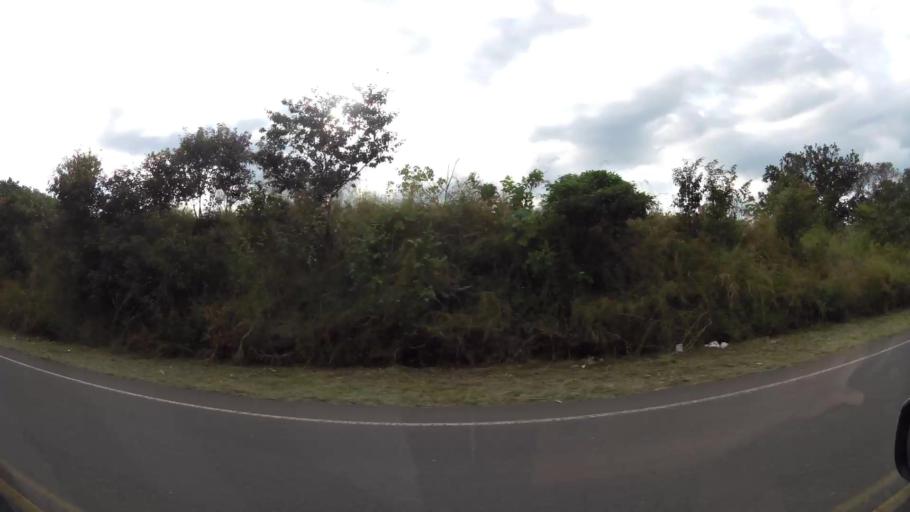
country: CR
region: Alajuela
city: Orotina
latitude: 9.8742
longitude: -84.5735
